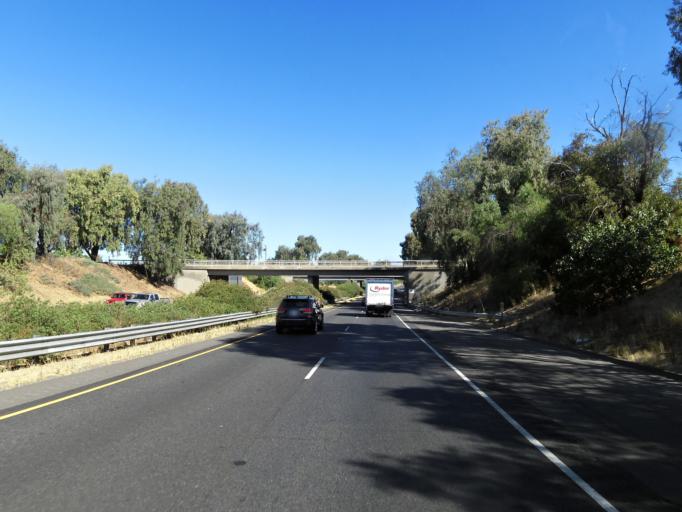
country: US
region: California
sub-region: Sacramento County
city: Galt
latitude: 38.2637
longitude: -121.2994
